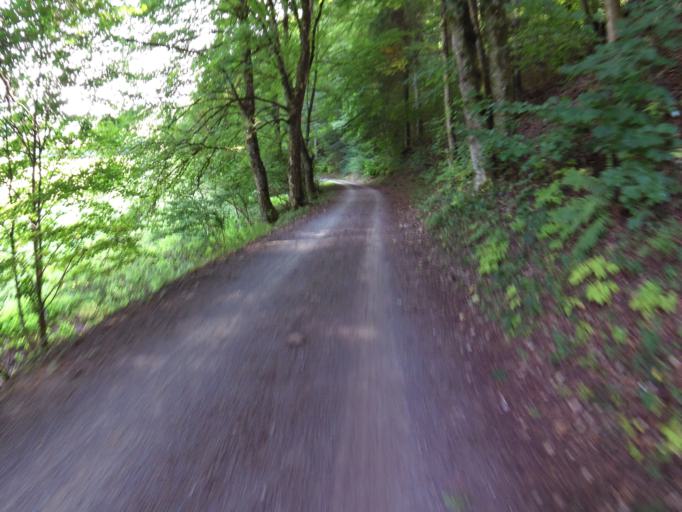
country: DE
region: Baden-Wuerttemberg
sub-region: Freiburg Region
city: Sulz am Neckar
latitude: 48.3942
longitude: 8.6529
